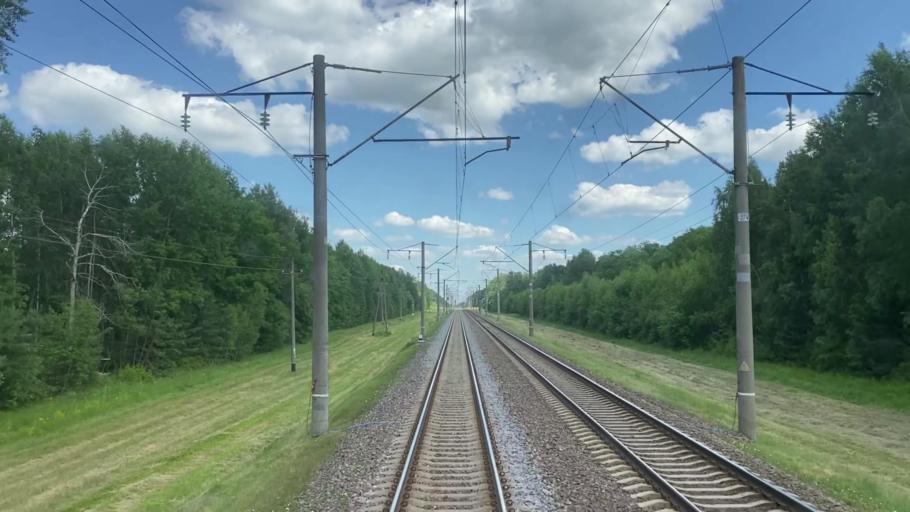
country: BY
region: Brest
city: Ivatsevichy
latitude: 52.7396
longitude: 25.3719
